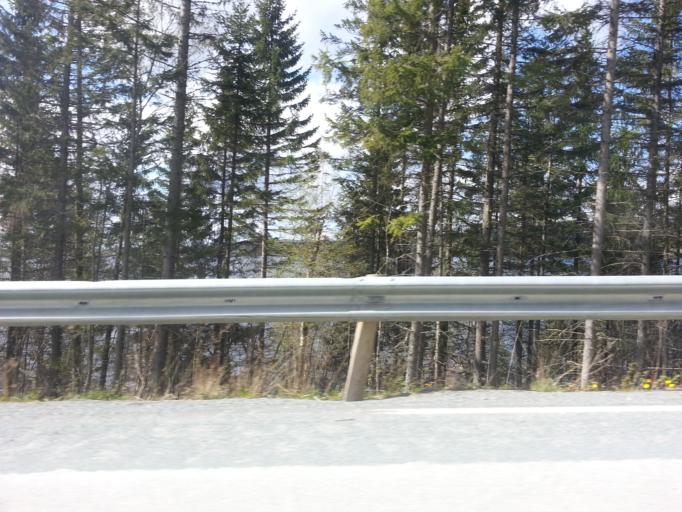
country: NO
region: Nord-Trondelag
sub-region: Levanger
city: Skogn
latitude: 63.6201
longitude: 11.1589
